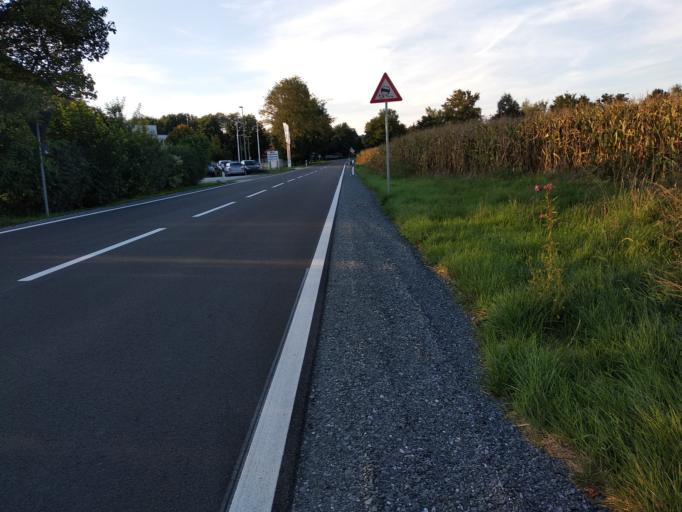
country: DE
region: Bavaria
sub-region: Upper Bavaria
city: Steinhoring
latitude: 48.0859
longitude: 12.0357
